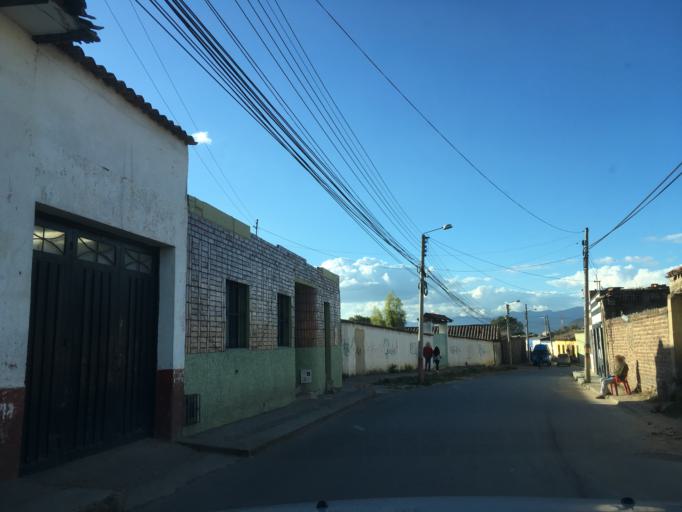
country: CO
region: Boyaca
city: Sogamoso
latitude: 5.7095
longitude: -72.9265
